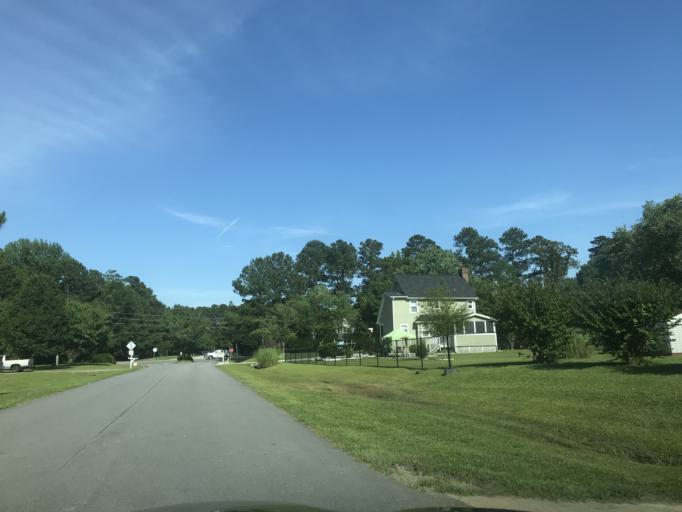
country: US
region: North Carolina
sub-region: Johnston County
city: Clayton
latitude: 35.5913
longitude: -78.5380
